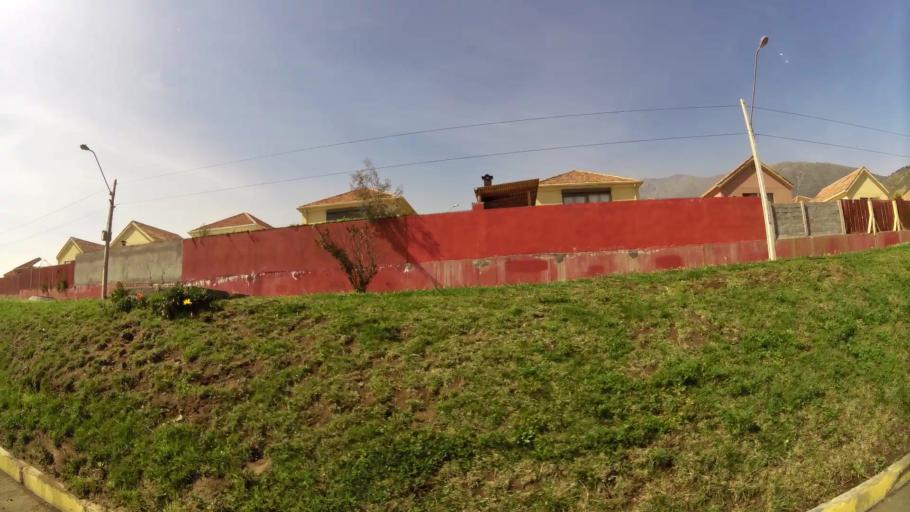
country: CL
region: Santiago Metropolitan
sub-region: Provincia de Cordillera
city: Puente Alto
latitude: -33.5352
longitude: -70.5418
